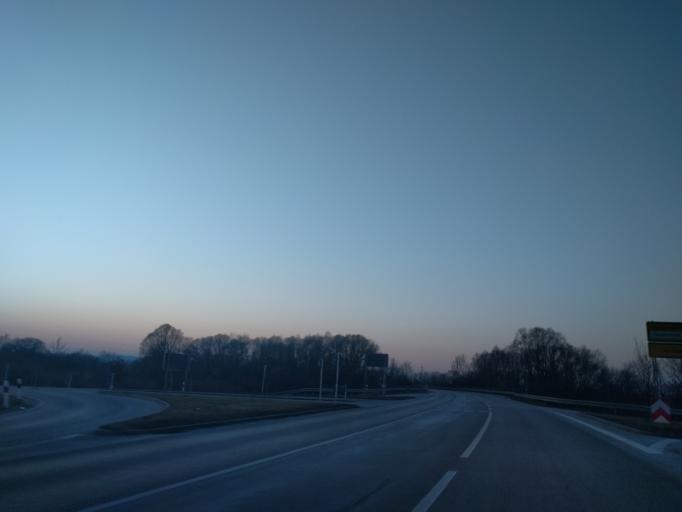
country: DE
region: Bavaria
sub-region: Swabia
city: Donauwoerth
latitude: 48.7033
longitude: 10.7855
